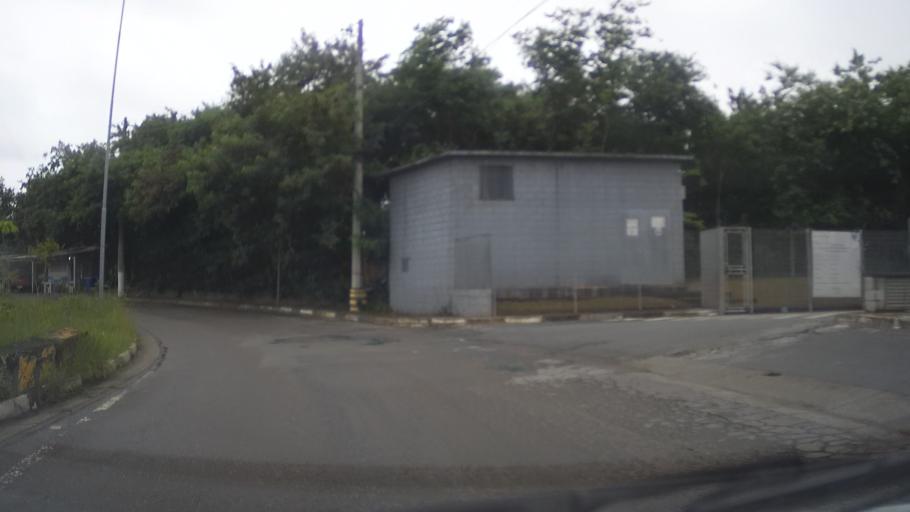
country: BR
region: Sao Paulo
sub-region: Guarulhos
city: Guarulhos
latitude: -23.4900
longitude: -46.5391
